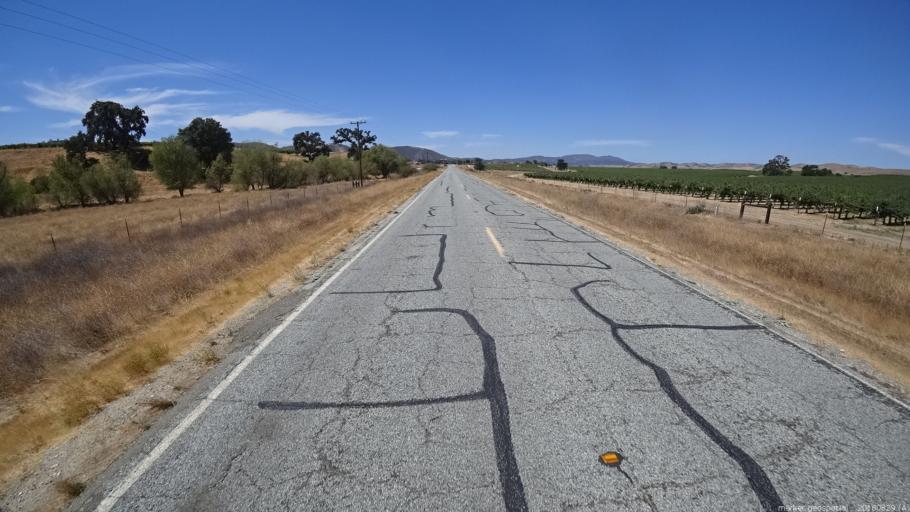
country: US
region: California
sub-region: San Luis Obispo County
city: Lake Nacimiento
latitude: 35.8727
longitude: -120.8735
